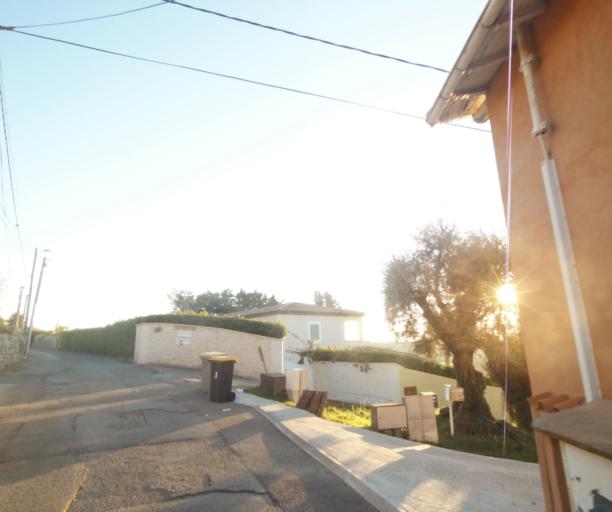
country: FR
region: Provence-Alpes-Cote d'Azur
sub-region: Departement des Alpes-Maritimes
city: Vallauris
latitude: 43.5865
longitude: 7.0714
